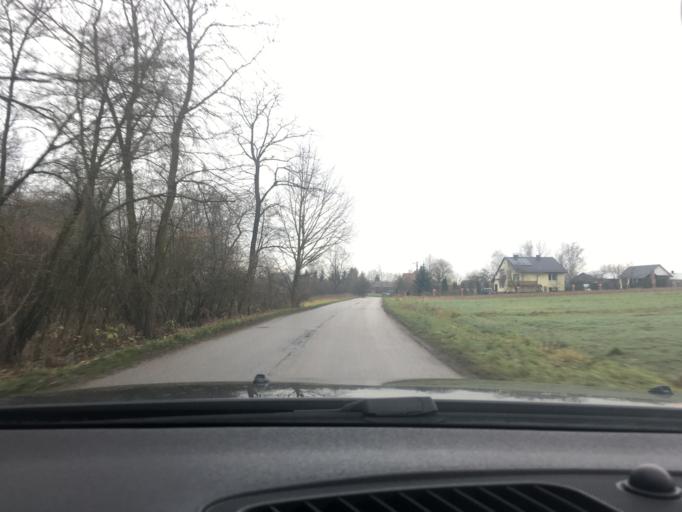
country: PL
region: Swietokrzyskie
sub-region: Powiat jedrzejowski
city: Imielno
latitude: 50.6412
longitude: 20.4091
